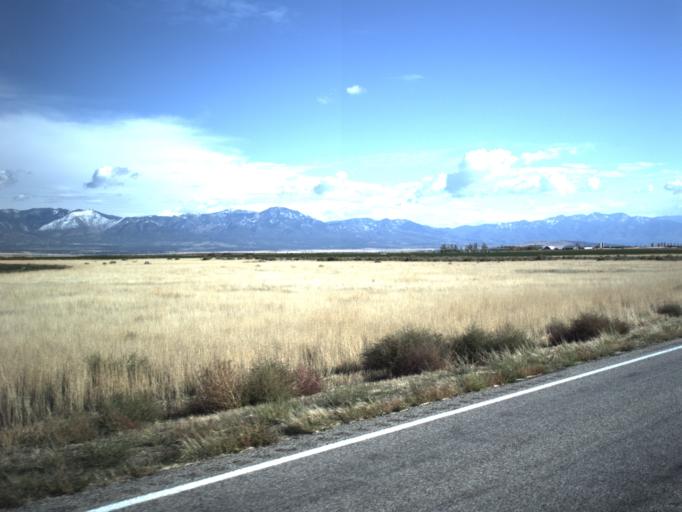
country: US
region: Utah
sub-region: Millard County
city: Fillmore
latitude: 39.1865
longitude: -112.4101
